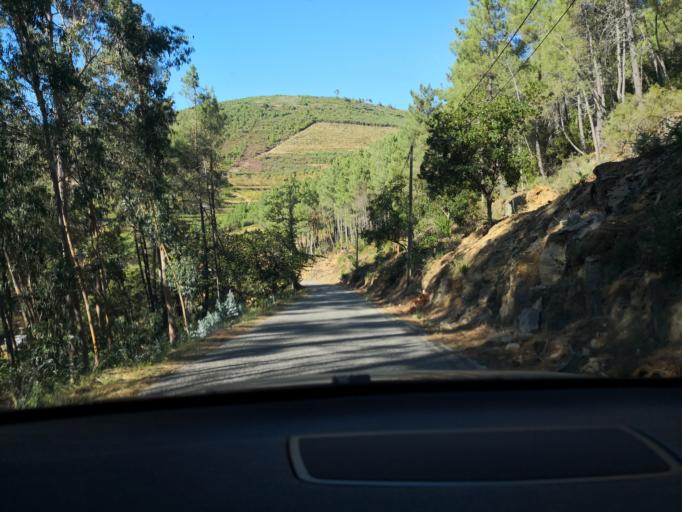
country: PT
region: Vila Real
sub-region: Sabrosa
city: Vilela
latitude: 41.2230
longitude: -7.5820
